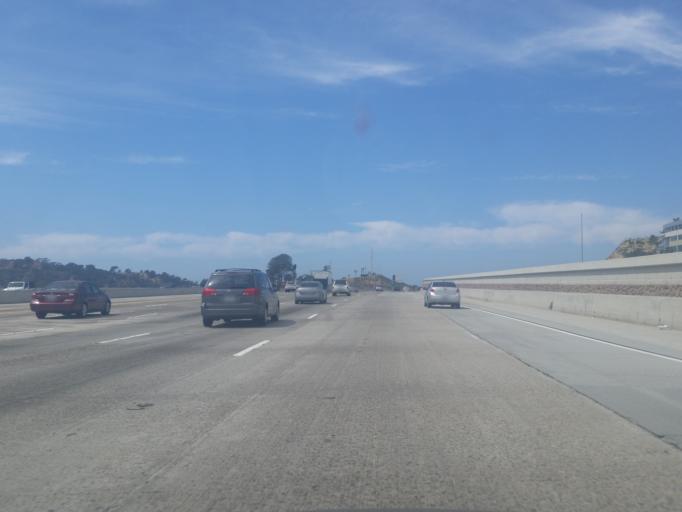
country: US
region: California
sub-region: San Diego County
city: Del Mar
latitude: 32.9167
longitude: -117.2326
